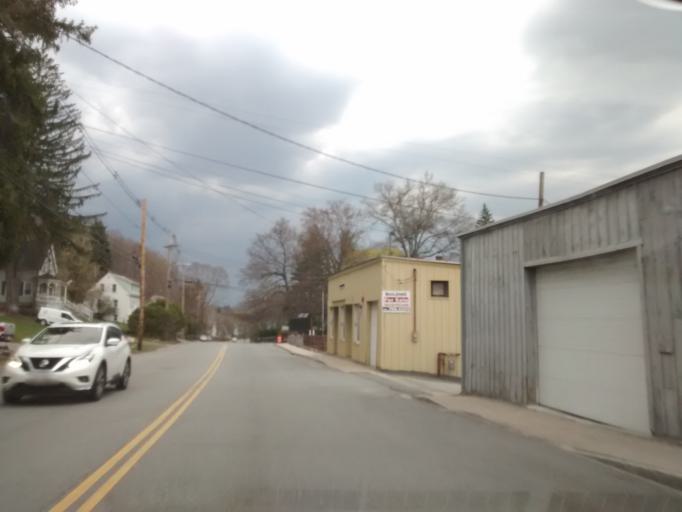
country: US
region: Massachusetts
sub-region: Worcester County
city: Millbury
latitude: 42.1815
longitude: -71.7699
